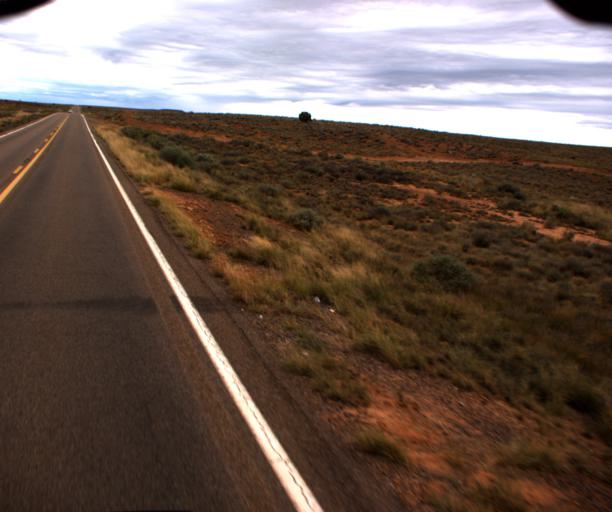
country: US
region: Arizona
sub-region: Navajo County
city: Holbrook
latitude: 34.7761
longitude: -110.1289
